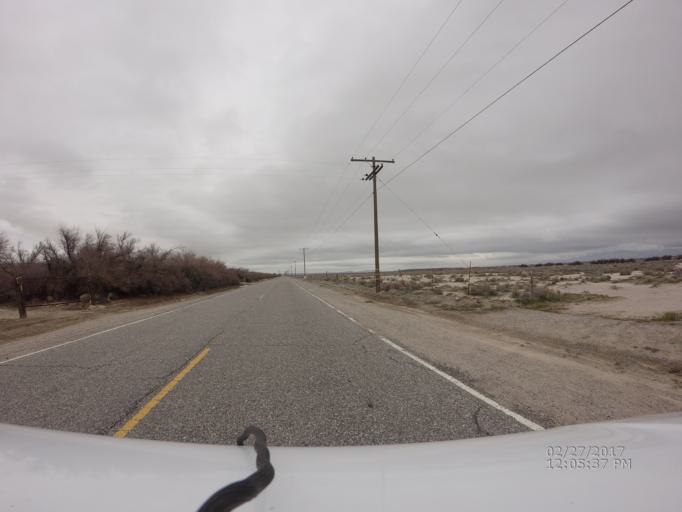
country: US
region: California
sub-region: Los Angeles County
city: Lancaster
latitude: 34.7625
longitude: -118.1579
